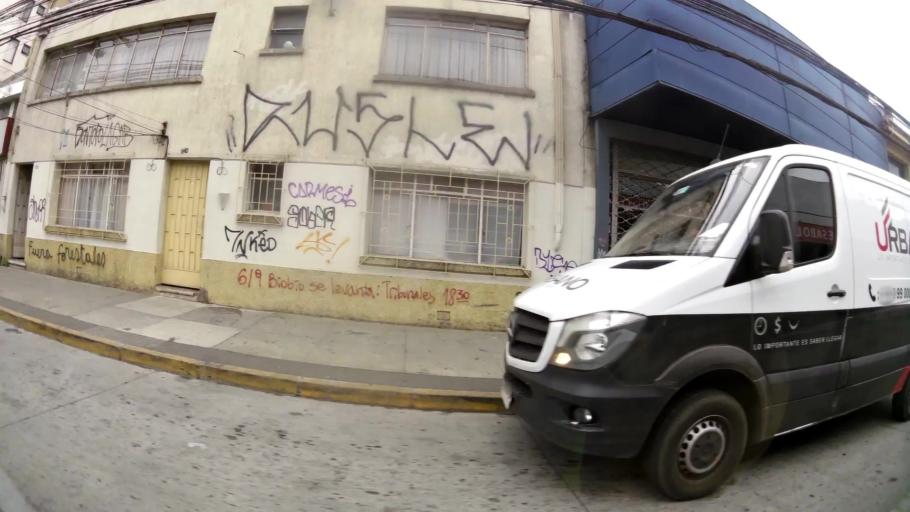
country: CL
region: Biobio
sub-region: Provincia de Concepcion
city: Concepcion
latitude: -36.8219
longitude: -73.0455
